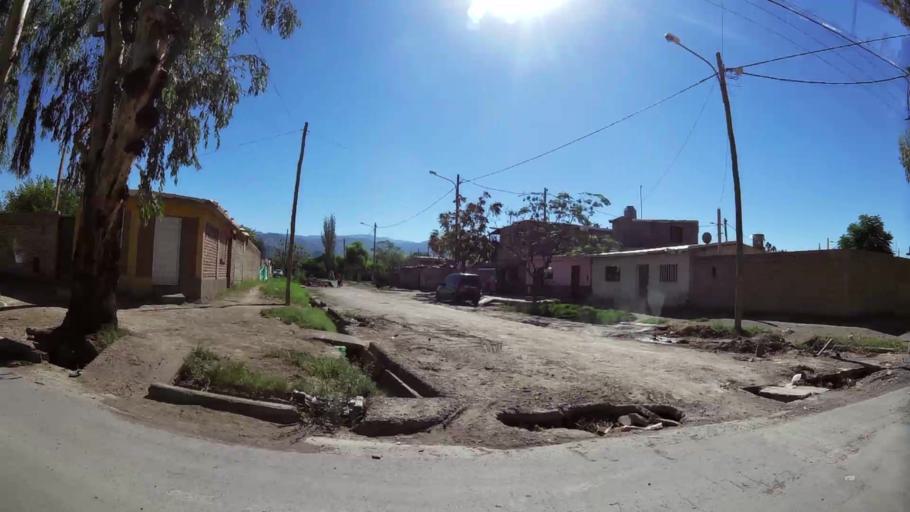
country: AR
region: Mendoza
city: Las Heras
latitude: -32.8311
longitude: -68.8168
